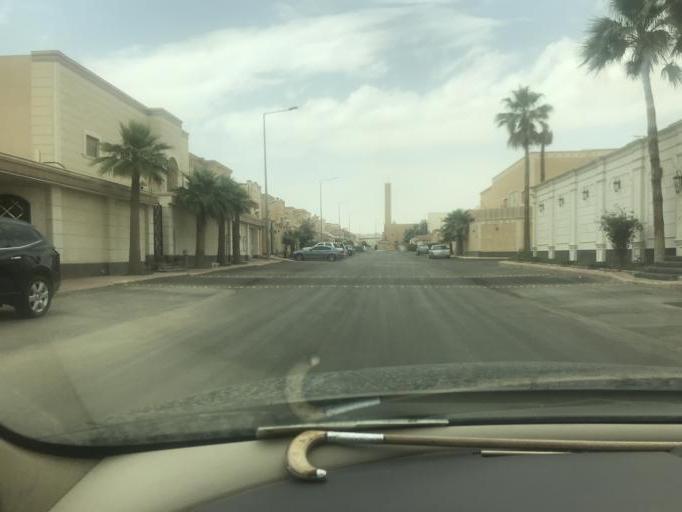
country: SA
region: Ar Riyad
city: Riyadh
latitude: 24.7912
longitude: 46.7128
